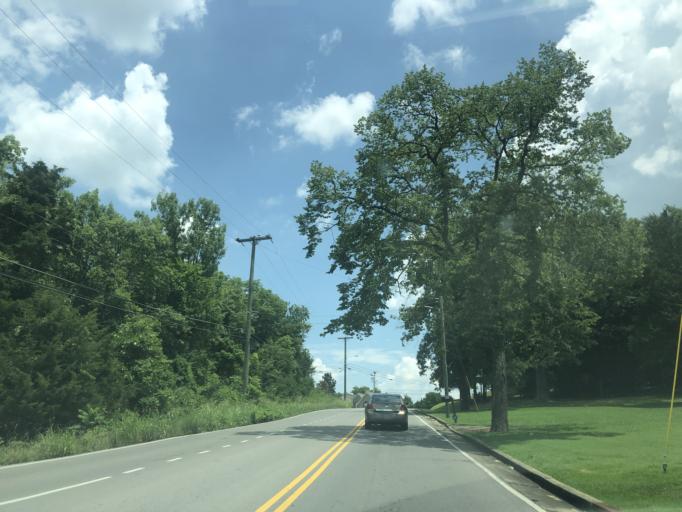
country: US
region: Tennessee
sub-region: Rutherford County
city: La Vergne
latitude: 36.0561
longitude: -86.6508
